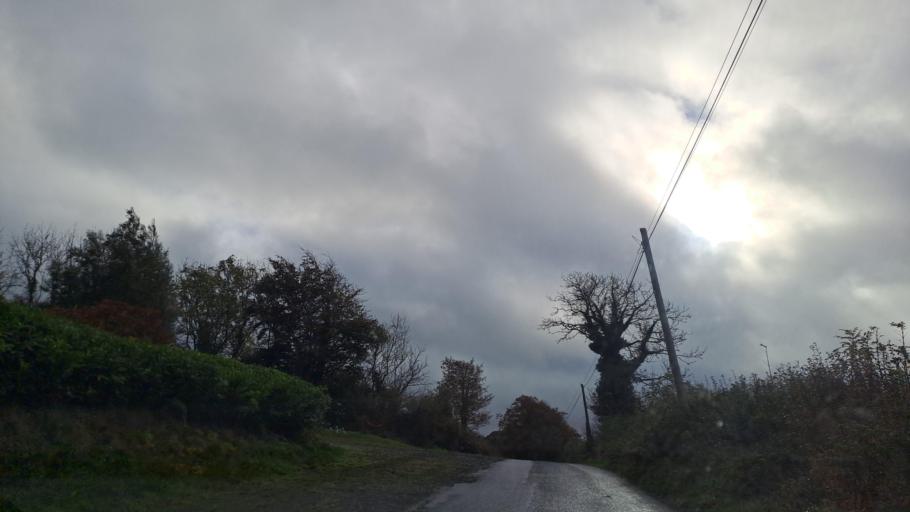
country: IE
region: Ulster
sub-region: An Cabhan
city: Bailieborough
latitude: 53.9863
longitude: -7.0114
